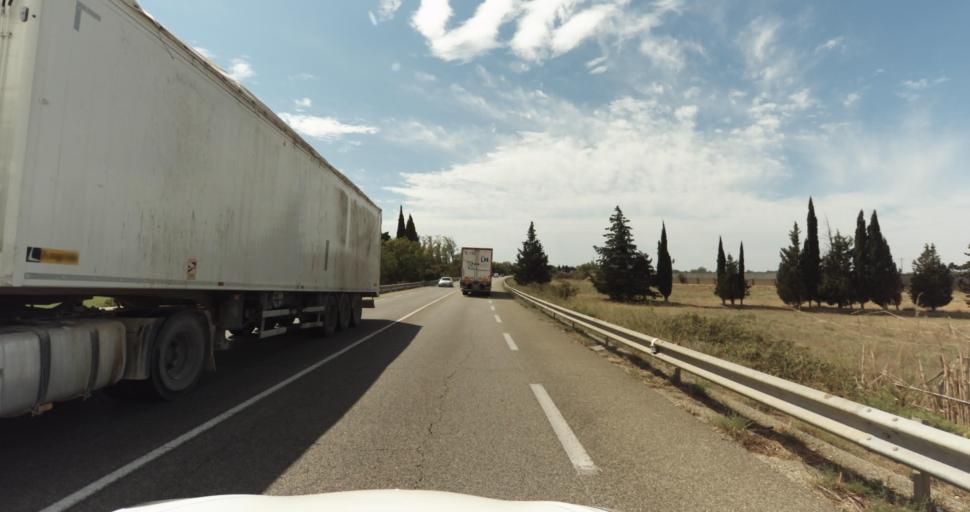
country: FR
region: Provence-Alpes-Cote d'Azur
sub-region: Departement des Bouches-du-Rhone
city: Miramas
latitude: 43.5761
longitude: 4.9843
